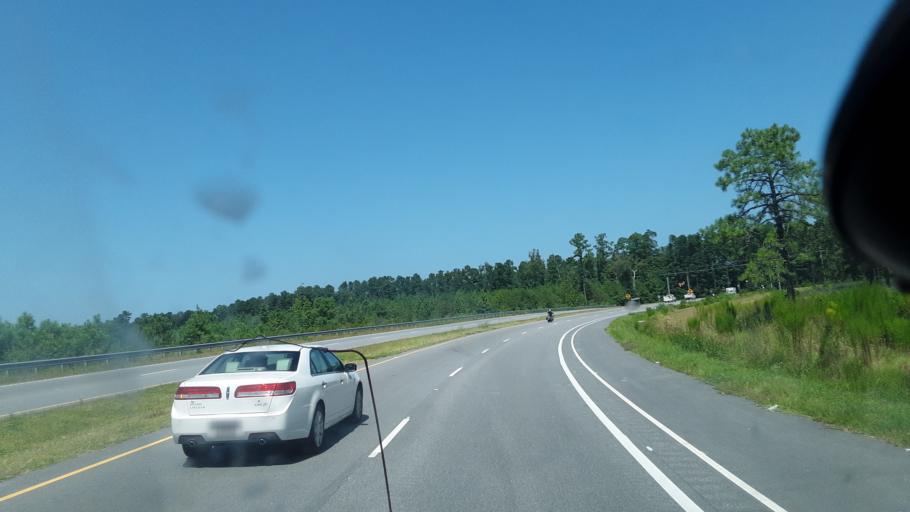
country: US
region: South Carolina
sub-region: Horry County
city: Red Hill
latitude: 33.8193
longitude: -78.9138
